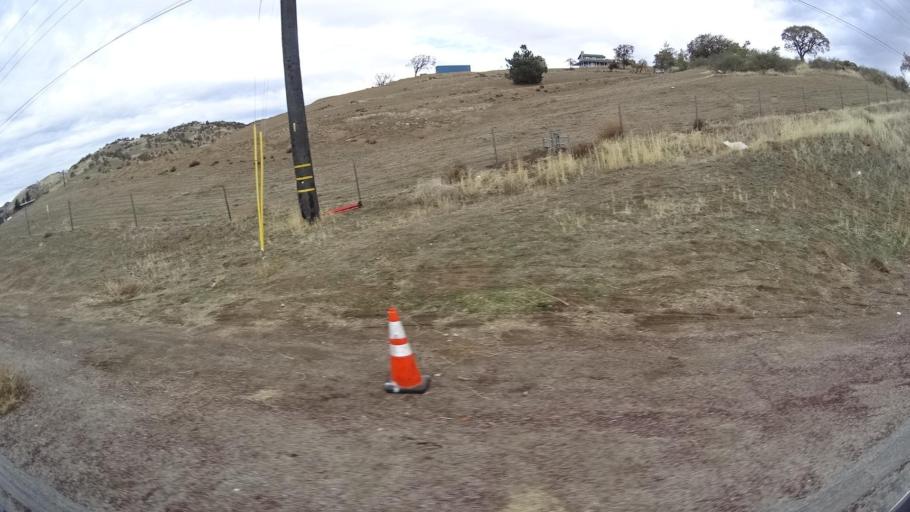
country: US
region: California
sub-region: Kern County
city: Golden Hills
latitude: 35.1136
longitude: -118.5247
